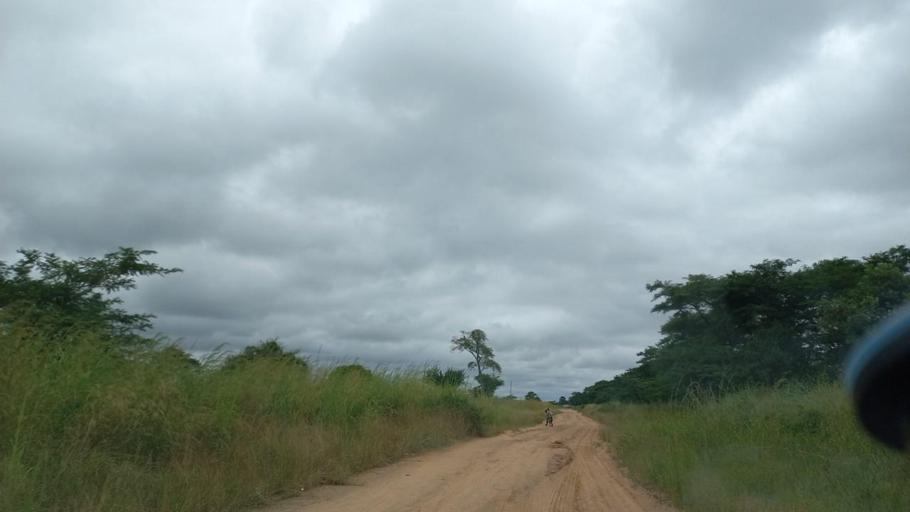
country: ZM
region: Lusaka
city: Lusaka
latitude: -15.2263
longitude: 28.3362
